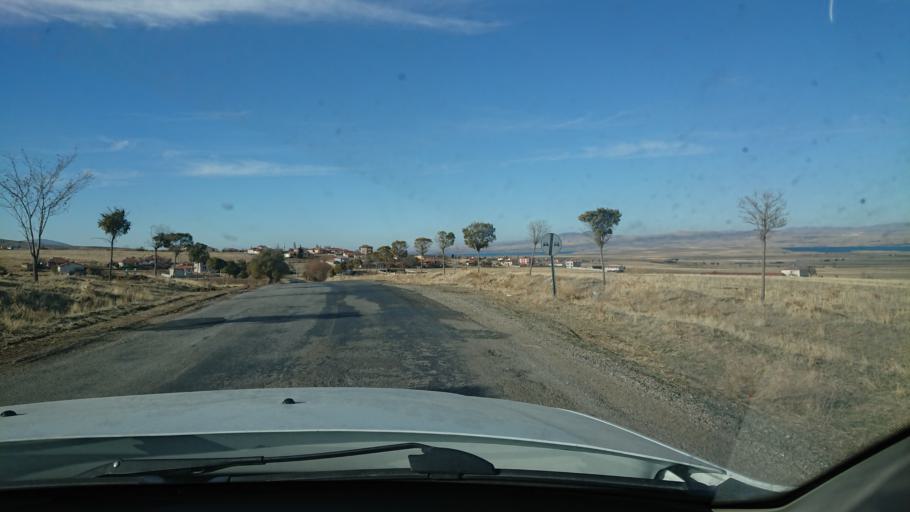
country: TR
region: Aksaray
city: Sariyahsi
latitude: 38.9753
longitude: 33.8577
